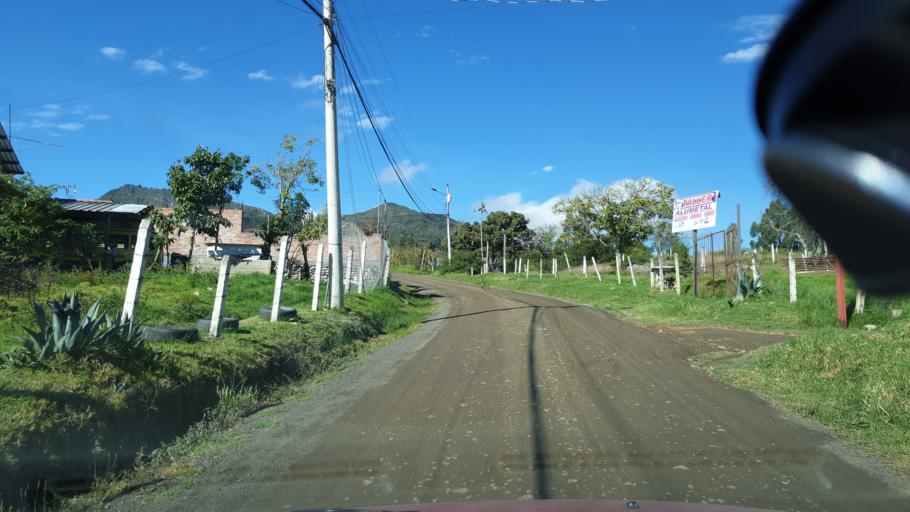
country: EC
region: Azuay
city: Llacao
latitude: -2.8623
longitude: -78.9148
